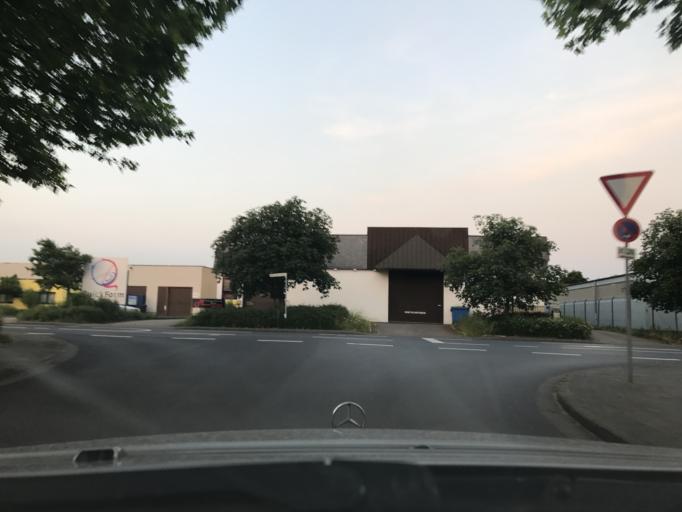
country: DE
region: North Rhine-Westphalia
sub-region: Regierungsbezirk Dusseldorf
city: Willich
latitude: 51.2729
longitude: 6.5157
